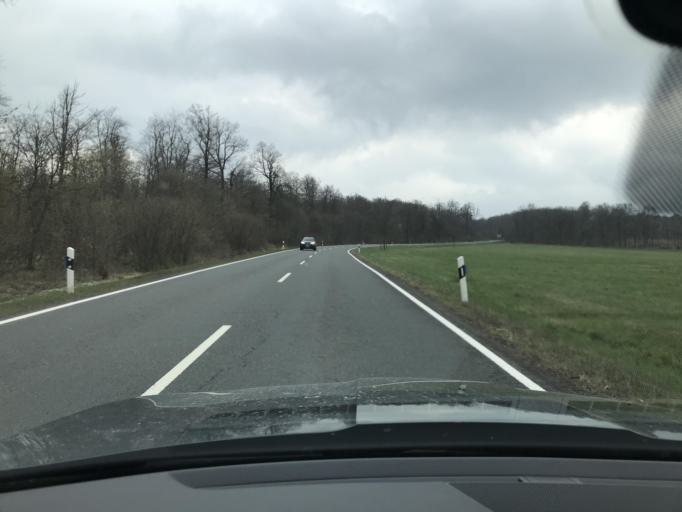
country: DE
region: Saxony-Anhalt
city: Harzgerode
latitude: 51.6190
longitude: 11.1609
